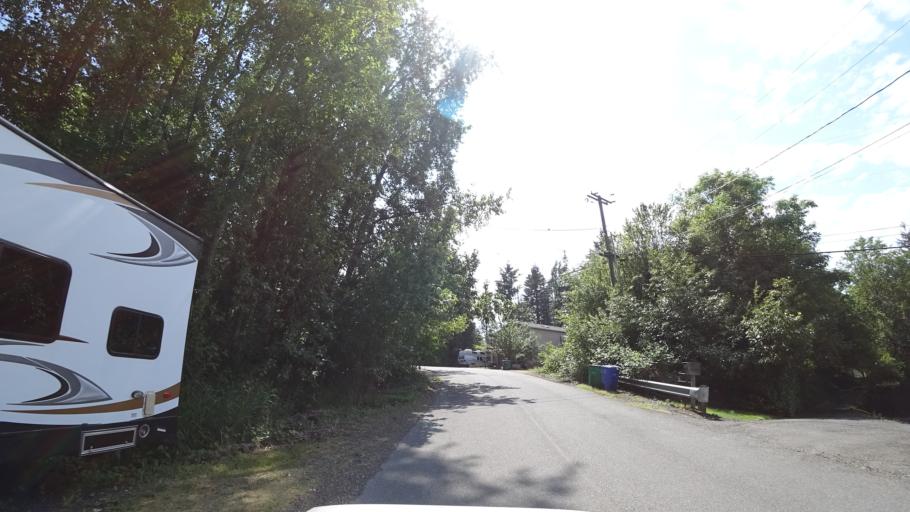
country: US
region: Oregon
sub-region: Washington County
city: Metzger
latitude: 45.4470
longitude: -122.7331
